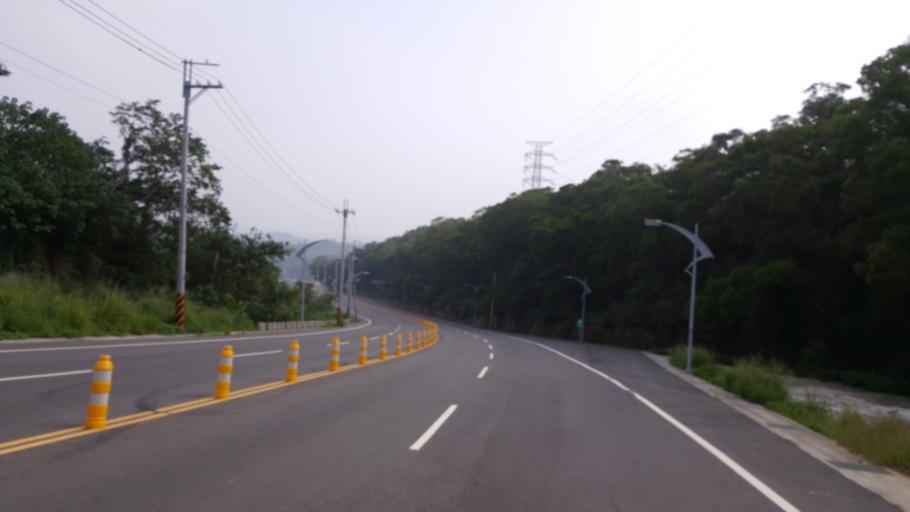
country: TW
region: Taiwan
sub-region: Hsinchu
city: Hsinchu
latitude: 24.7454
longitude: 120.9581
